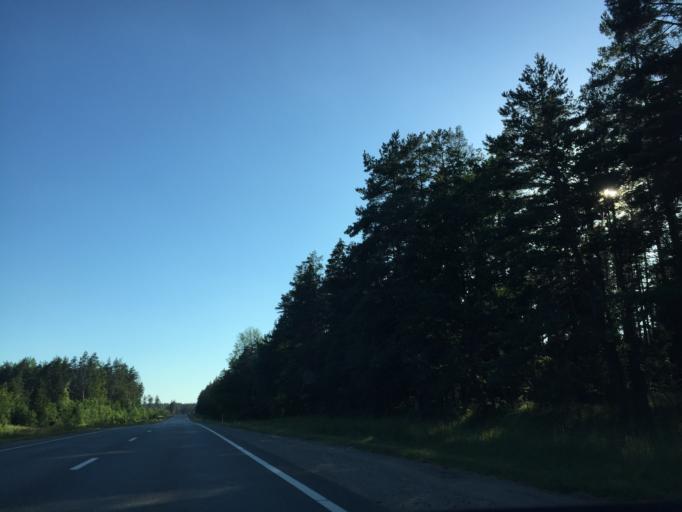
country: LV
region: Ventspils Rajons
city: Piltene
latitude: 57.3931
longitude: 21.8151
